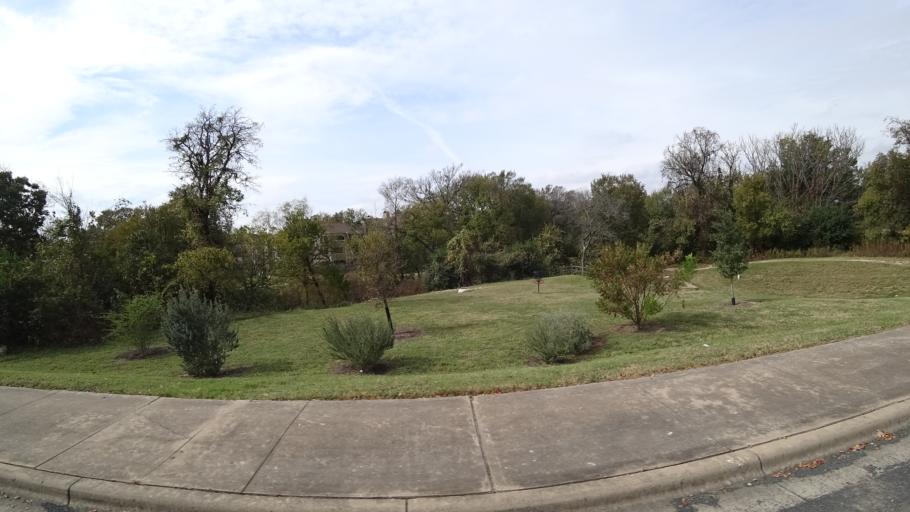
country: US
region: Texas
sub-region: Travis County
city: Wells Branch
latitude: 30.4342
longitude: -97.6713
